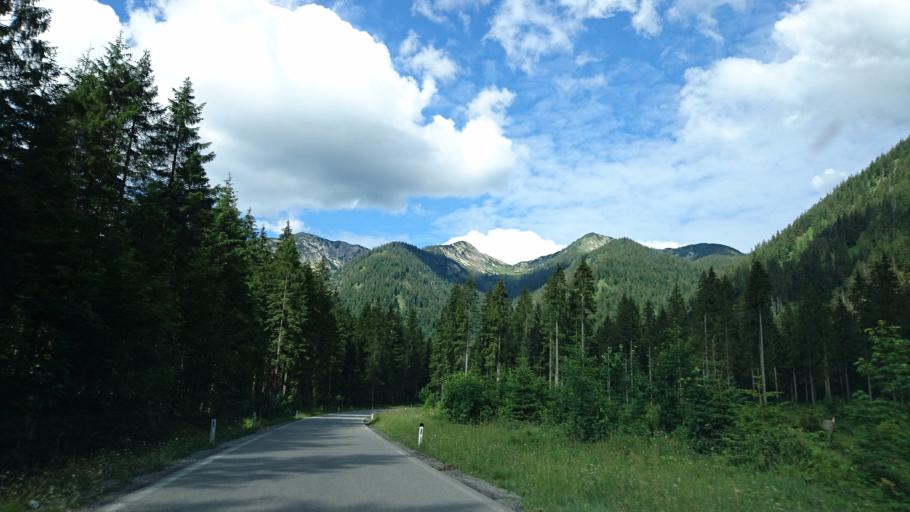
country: DE
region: Bavaria
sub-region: Swabia
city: Halblech
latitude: 47.5294
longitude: 10.8521
